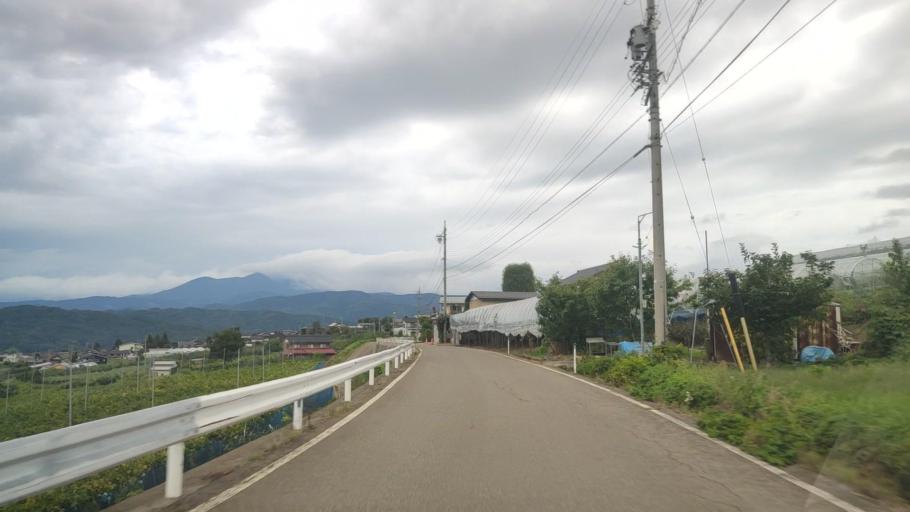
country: JP
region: Nagano
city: Nakano
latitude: 36.7792
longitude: 138.3747
